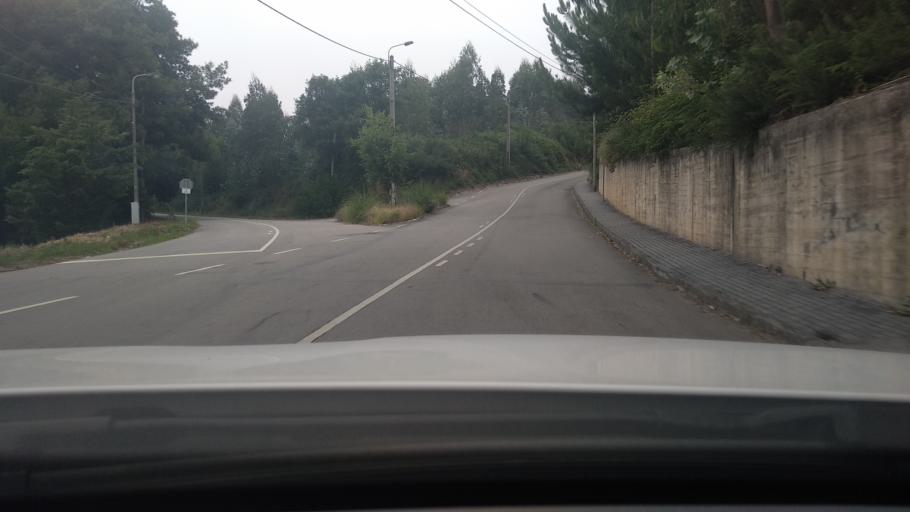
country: PT
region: Aveiro
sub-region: Espinho
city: Silvalde
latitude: 40.9981
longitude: -8.6282
